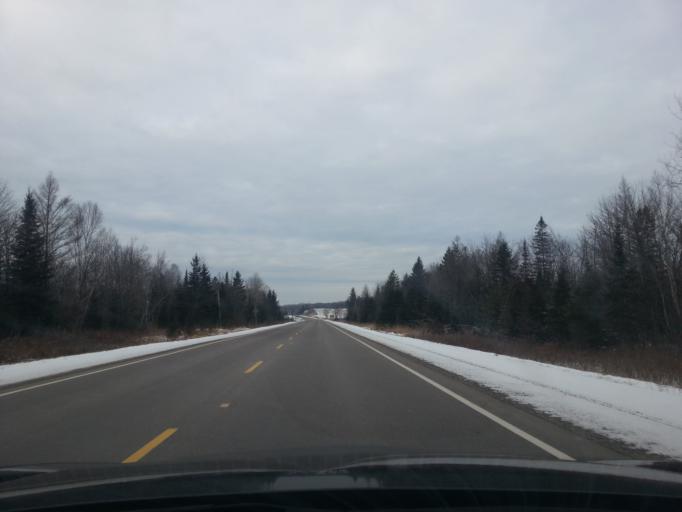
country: CA
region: Ontario
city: Skatepark
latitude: 44.7539
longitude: -76.8498
